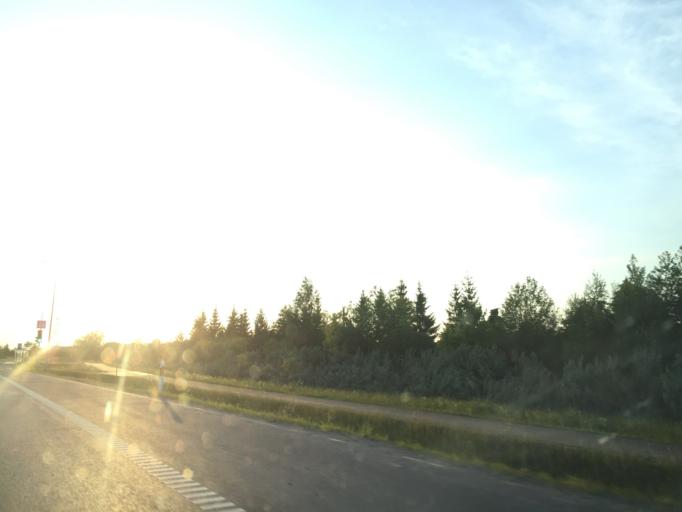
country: LT
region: Siauliu apskritis
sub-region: Siauliai
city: Siauliai
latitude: 55.9601
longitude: 23.2394
